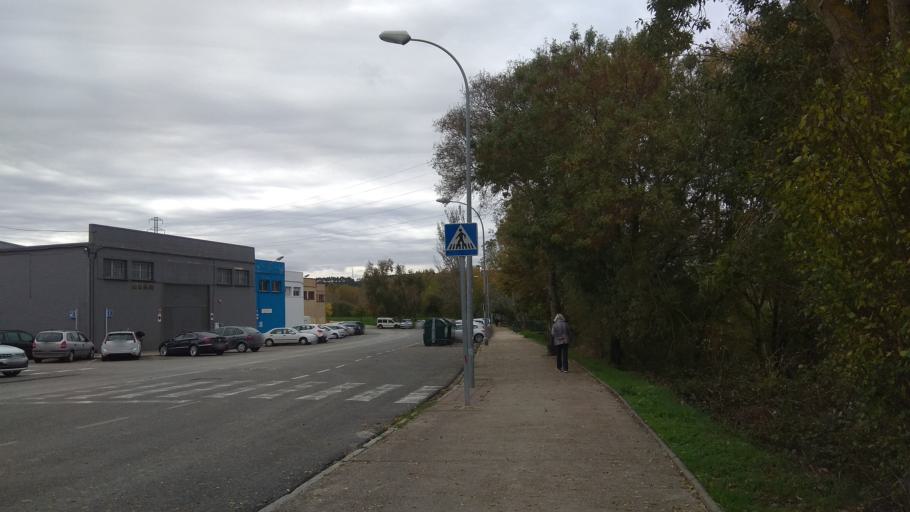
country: ES
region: Navarre
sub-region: Provincia de Navarra
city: Baranain
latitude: 42.8085
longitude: -1.6918
